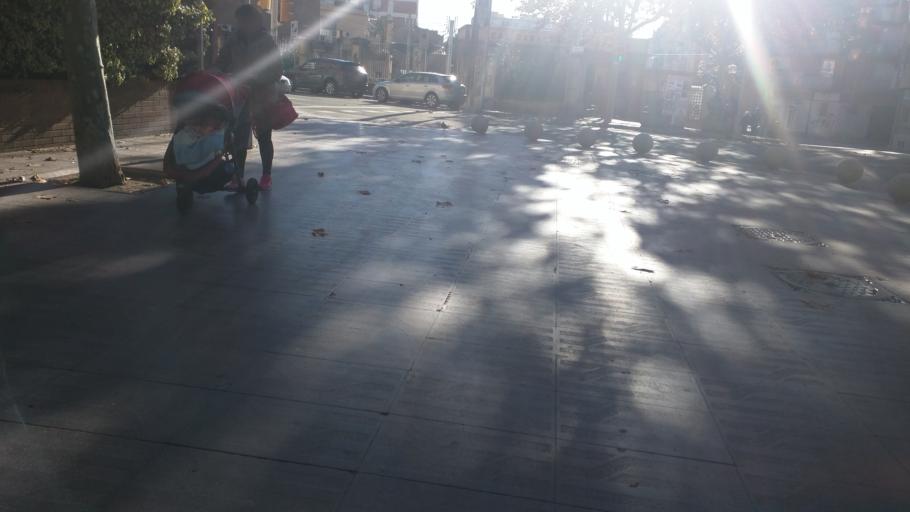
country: ES
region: Catalonia
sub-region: Provincia de Barcelona
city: Molins de Rei
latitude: 41.4100
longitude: 2.0170
